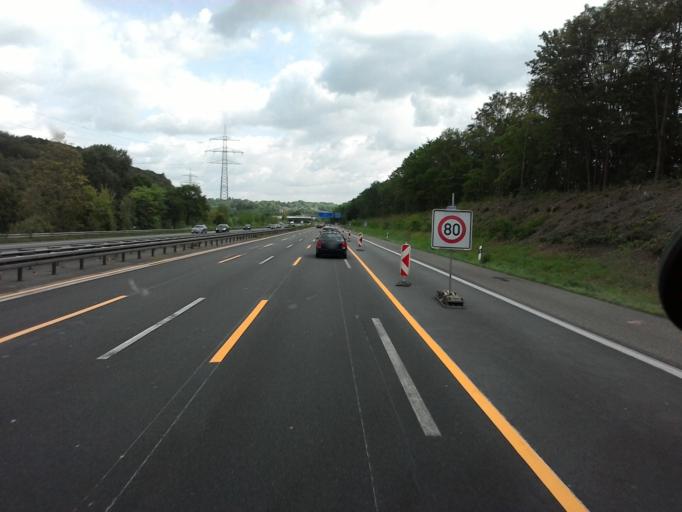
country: DE
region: North Rhine-Westphalia
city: Lohmar
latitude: 50.8452
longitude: 7.2087
